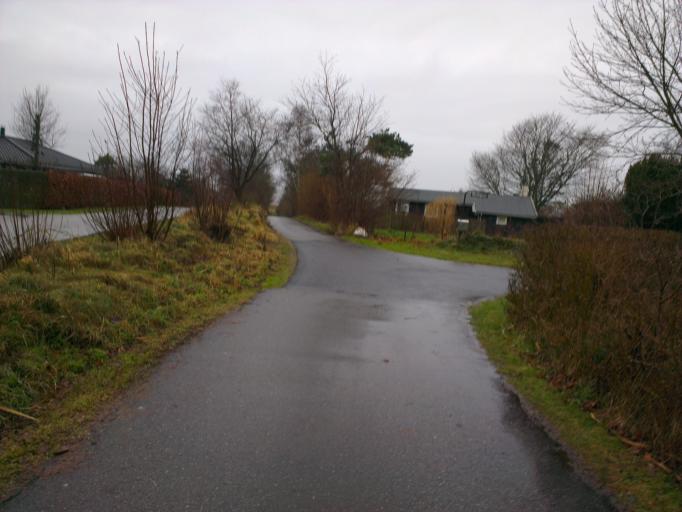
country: DK
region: Capital Region
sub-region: Frederikssund Kommune
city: Jaegerspris
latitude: 55.8340
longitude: 11.9557
